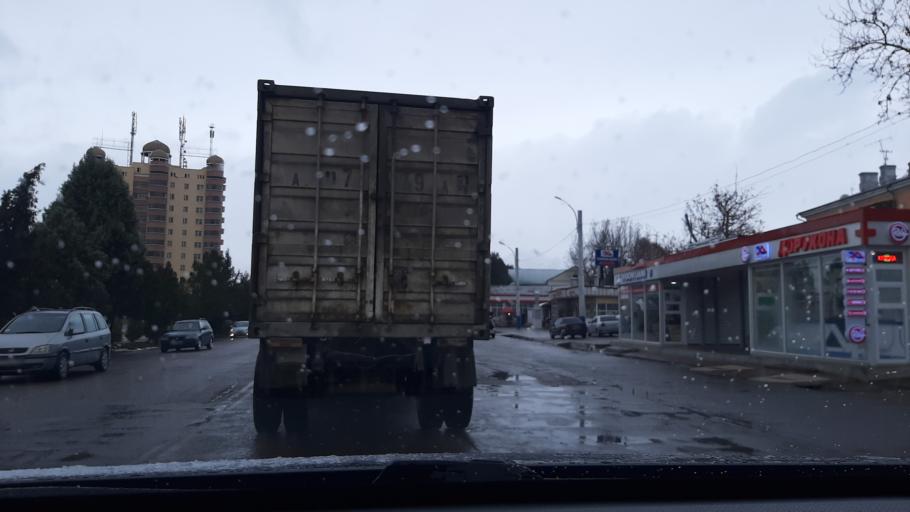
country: TJ
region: Viloyati Sughd
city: Khujand
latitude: 40.2717
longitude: 69.6437
